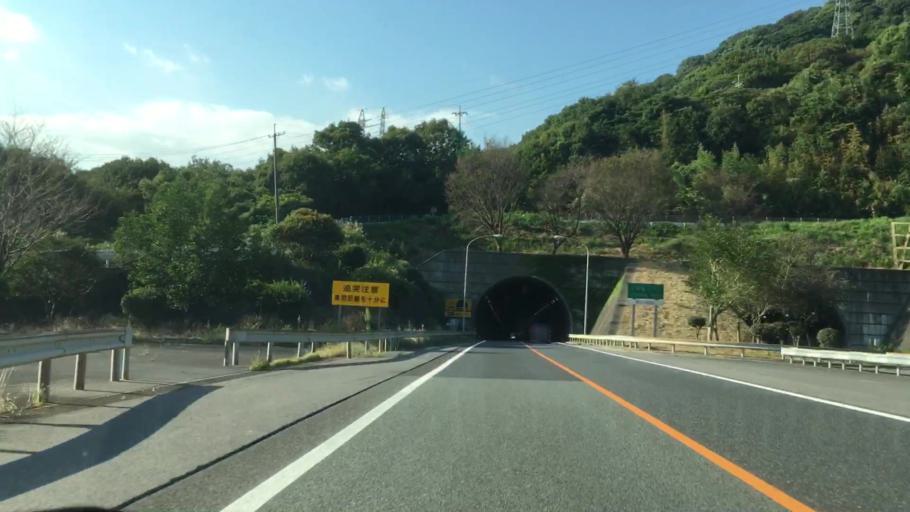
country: JP
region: Yamaguchi
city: Tokuyama
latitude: 34.0603
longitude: 131.8359
